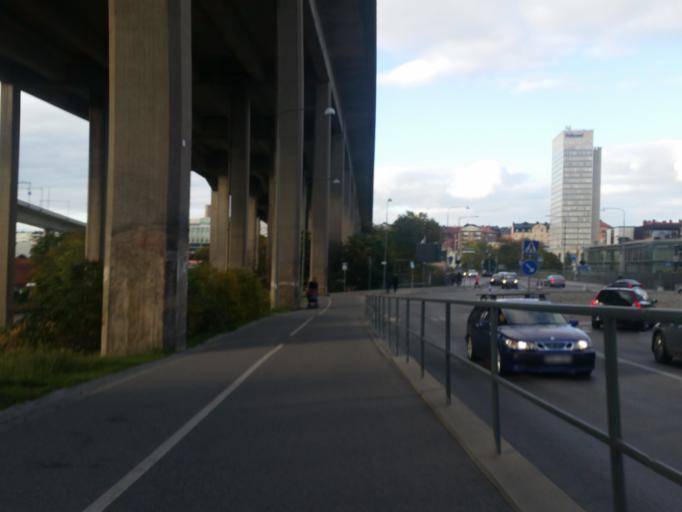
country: SE
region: Stockholm
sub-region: Stockholms Kommun
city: Arsta
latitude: 59.3023
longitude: 18.0802
